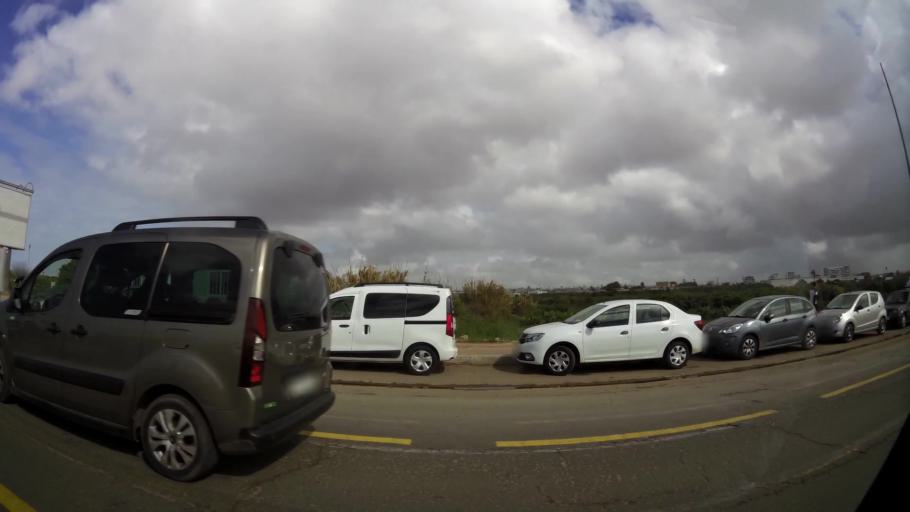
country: MA
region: Grand Casablanca
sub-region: Casablanca
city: Casablanca
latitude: 33.5800
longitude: -7.7034
